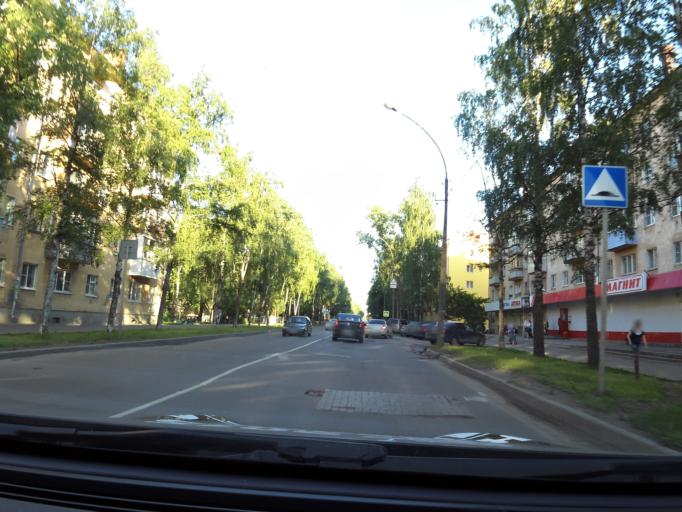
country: RU
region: Vologda
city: Vologda
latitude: 59.2070
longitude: 39.9071
